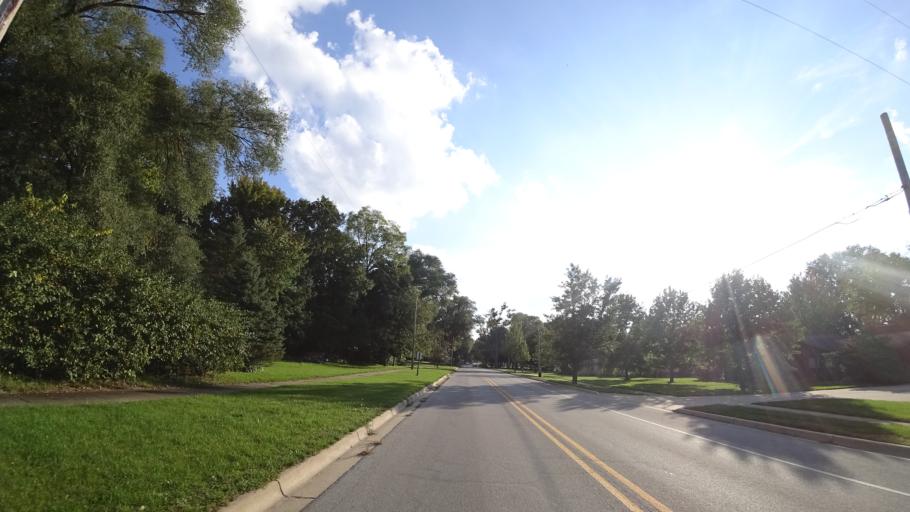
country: US
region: Michigan
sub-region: Saint Joseph County
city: Three Rivers
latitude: 41.9566
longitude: -85.6267
